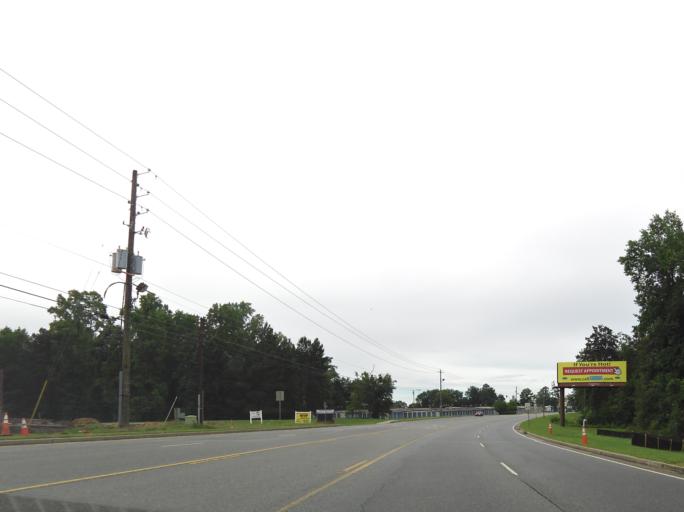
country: US
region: Georgia
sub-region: Lowndes County
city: Remerton
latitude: 30.8315
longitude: -83.3206
